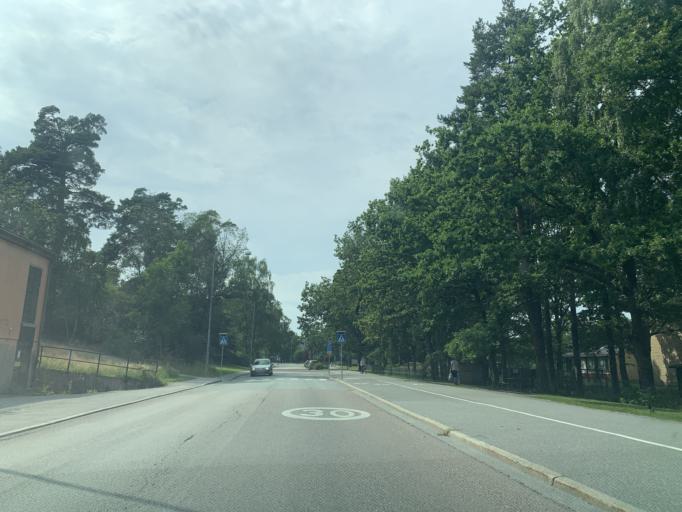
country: SE
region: Stockholm
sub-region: Norrtalje Kommun
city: Bergshamra
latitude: 59.3820
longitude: 18.0317
